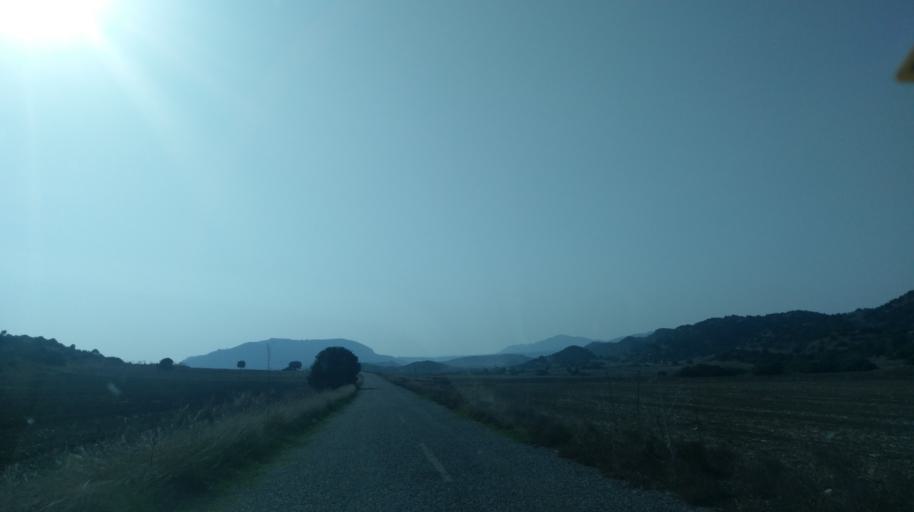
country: CY
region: Ammochostos
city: Rizokarpaso
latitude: 35.5507
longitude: 34.3530
